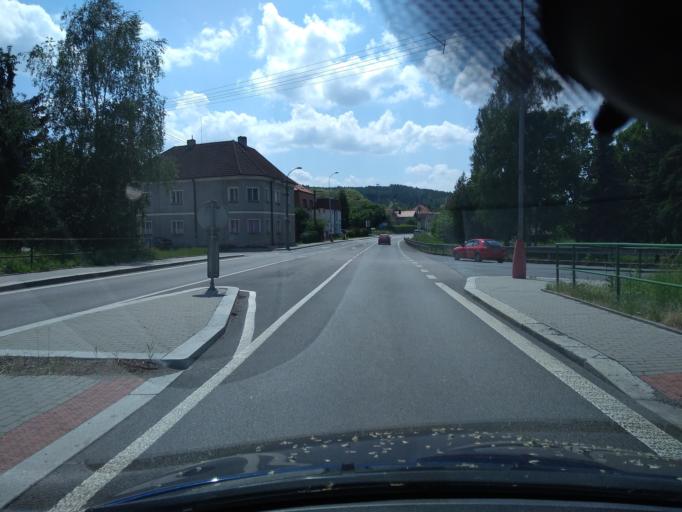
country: CZ
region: Plzensky
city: Svihov
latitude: 49.4791
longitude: 13.2914
